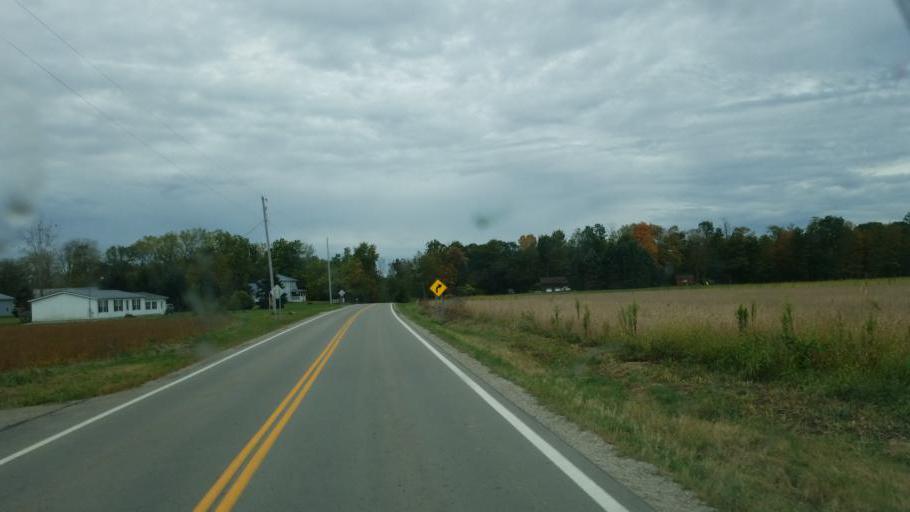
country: US
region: Ohio
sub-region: Huron County
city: Wakeman
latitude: 41.2459
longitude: -82.3961
